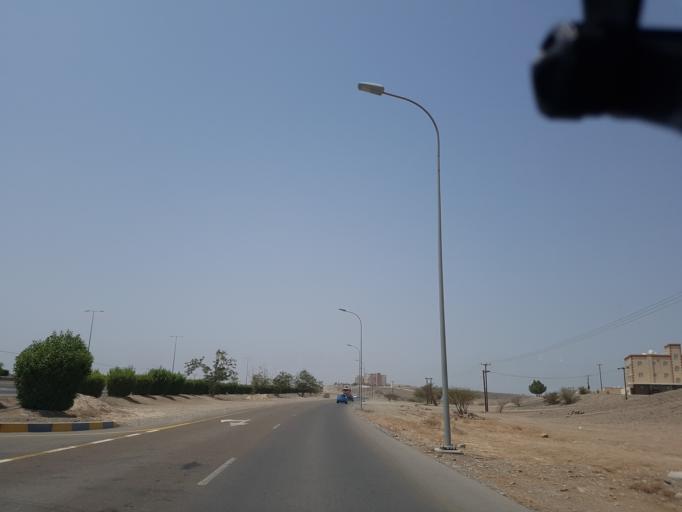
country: OM
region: Al Batinah
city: Al Liwa'
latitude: 24.4131
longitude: 56.5985
